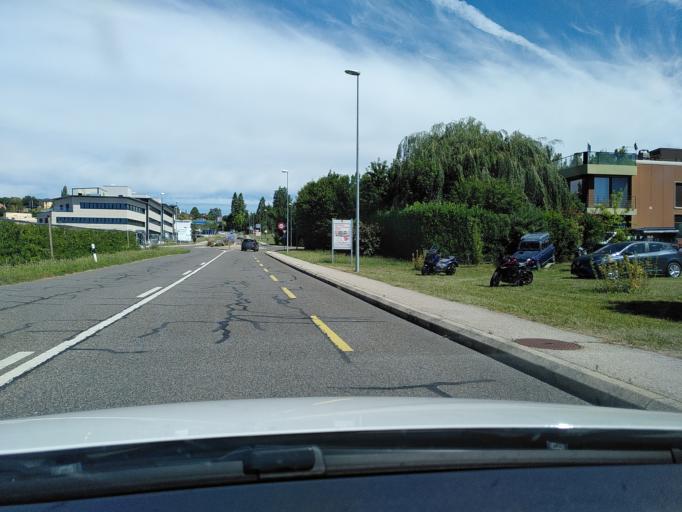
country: CH
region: Vaud
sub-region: Morges District
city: Aubonne
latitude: 46.4876
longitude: 6.3996
